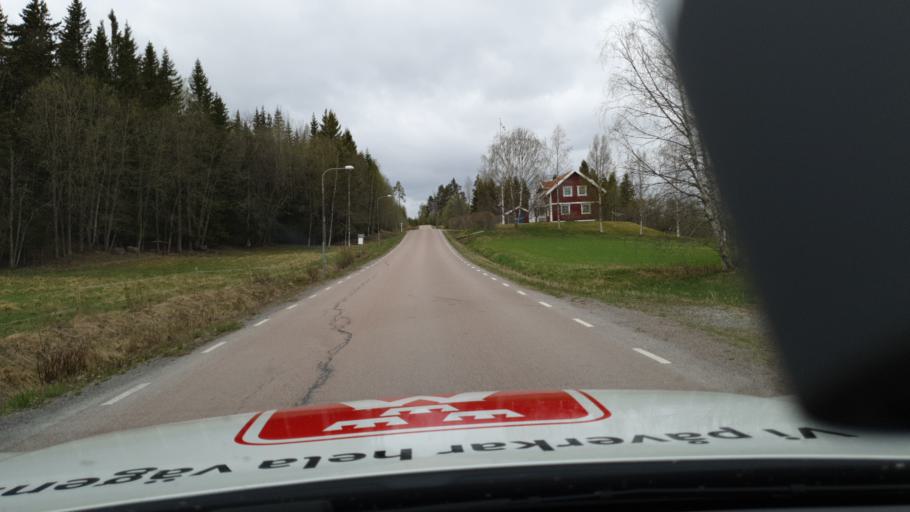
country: SE
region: Jaemtland
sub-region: OEstersunds Kommun
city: Lit
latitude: 63.3030
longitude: 14.9440
